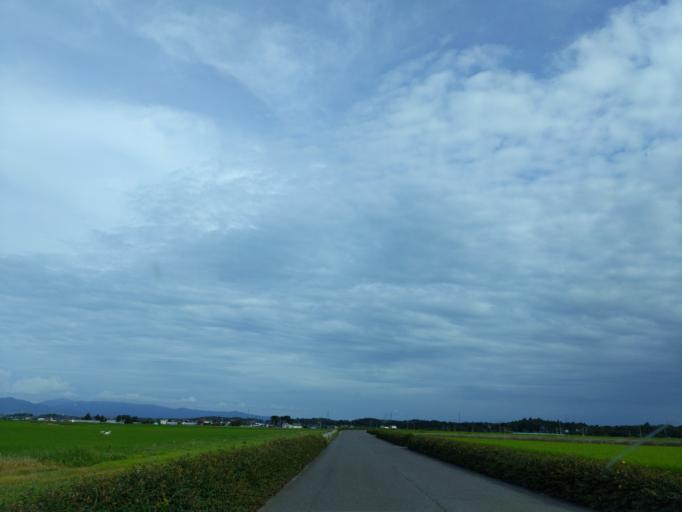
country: JP
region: Fukushima
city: Sukagawa
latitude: 37.3358
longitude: 140.3128
